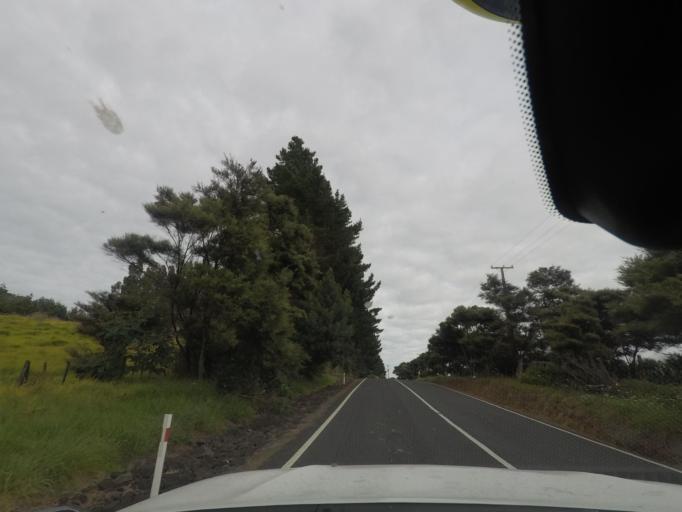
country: NZ
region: Auckland
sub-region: Auckland
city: Parakai
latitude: -36.5209
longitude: 174.2713
